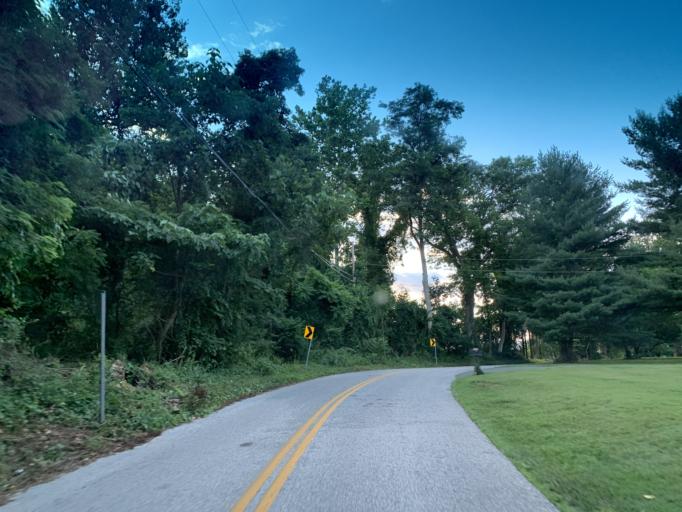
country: US
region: Maryland
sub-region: Harford County
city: Aberdeen
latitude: 39.5358
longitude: -76.1567
